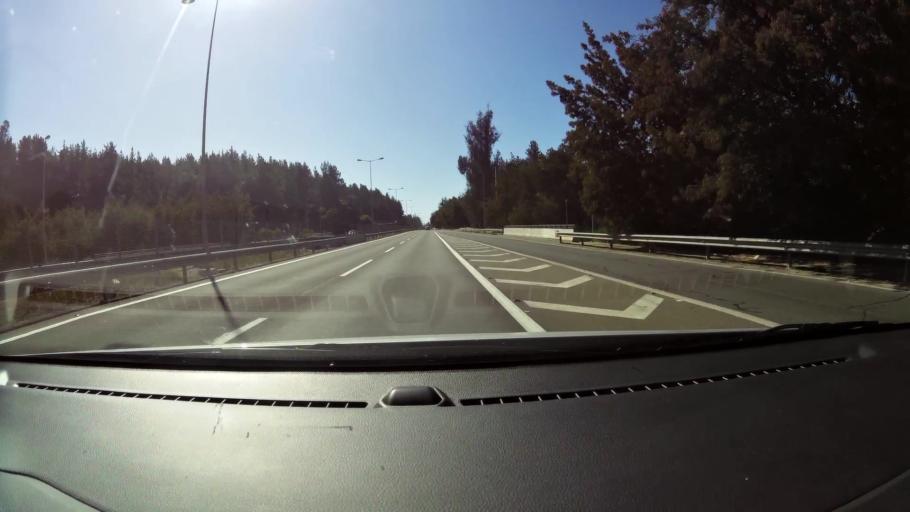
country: CL
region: Valparaiso
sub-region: Provincia de Valparaiso
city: Vina del Mar
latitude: -33.1626
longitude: -71.5392
